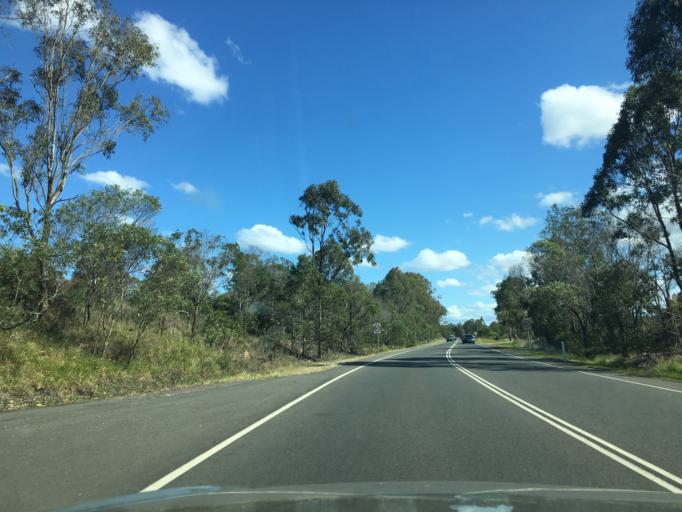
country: AU
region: Queensland
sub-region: Logan
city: Waterford West
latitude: -27.7013
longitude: 153.1479
